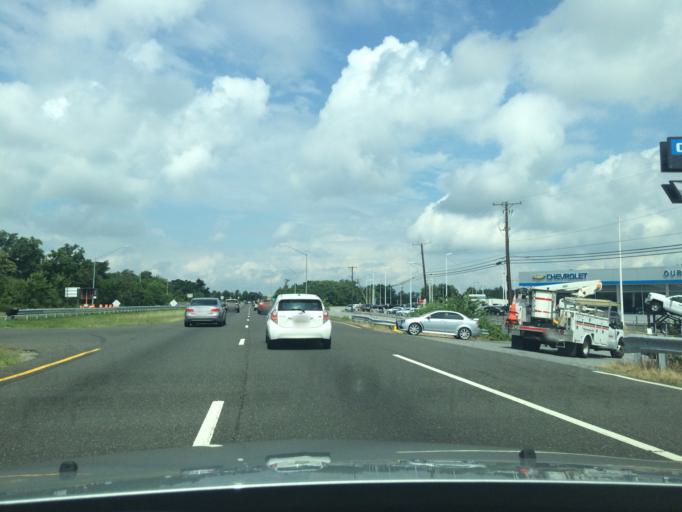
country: US
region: Maryland
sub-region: Prince George's County
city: Silver Hill
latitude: 38.8309
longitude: -76.9338
